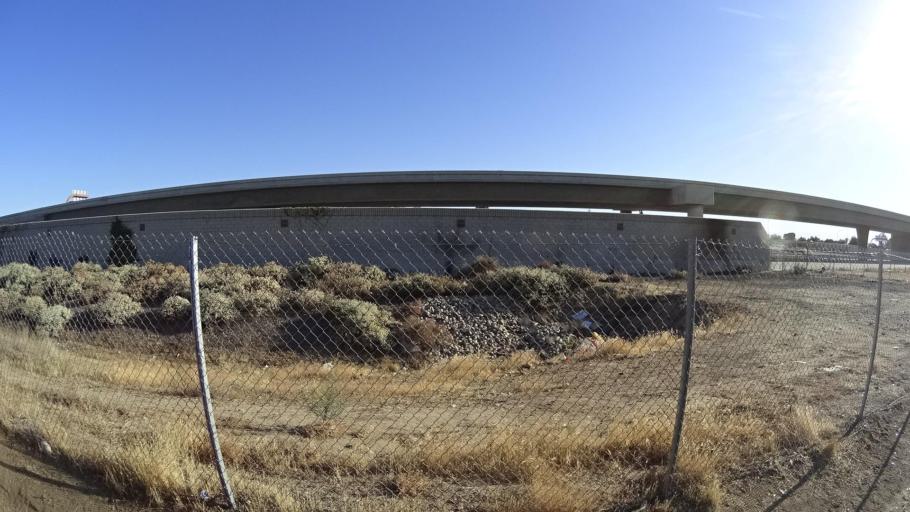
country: US
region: California
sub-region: Fresno County
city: Fresno
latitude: 36.7541
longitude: -119.7637
